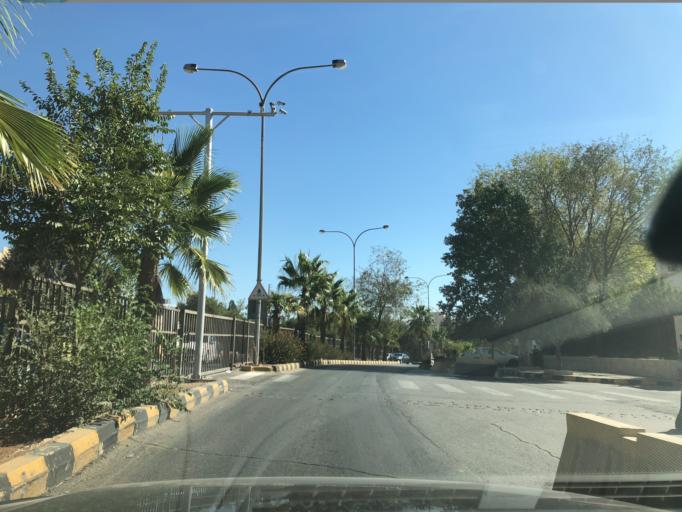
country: JO
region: Amman
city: Amman
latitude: 31.9789
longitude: 35.9062
